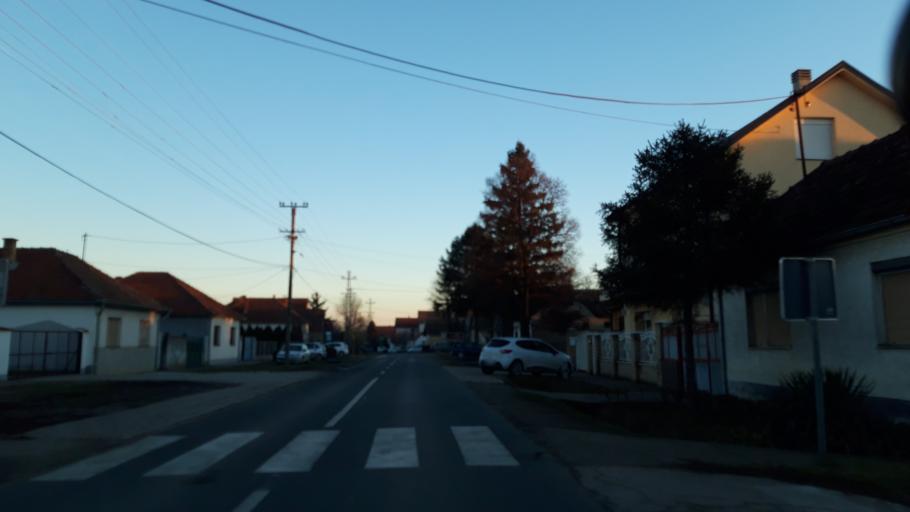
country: RS
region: Autonomna Pokrajina Vojvodina
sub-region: Sremski Okrug
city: Ingija
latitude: 45.0485
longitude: 20.0693
